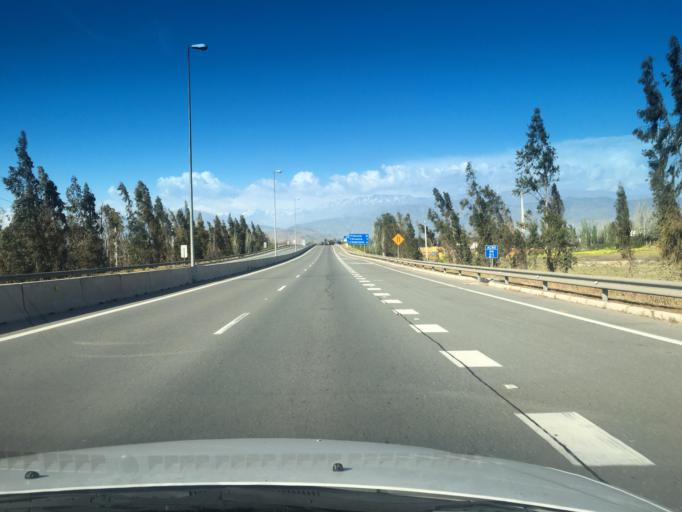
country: CL
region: Santiago Metropolitan
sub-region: Provincia de Chacabuco
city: Chicureo Abajo
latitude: -33.2986
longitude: -70.7267
